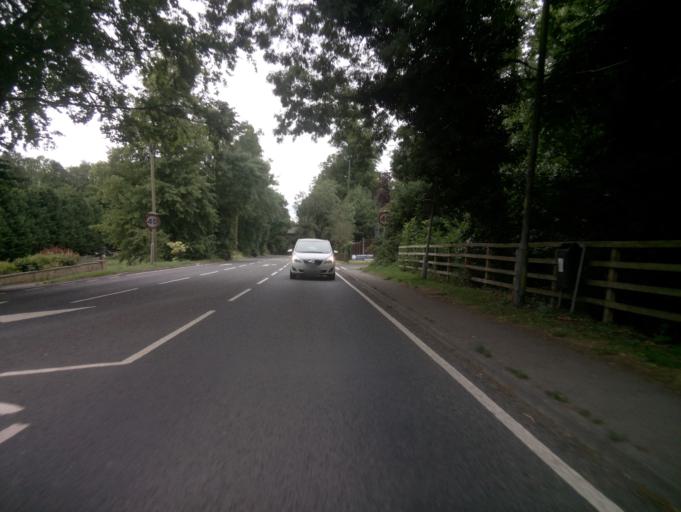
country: GB
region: England
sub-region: Worcestershire
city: Fernhill Heath
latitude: 52.2258
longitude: -2.2073
